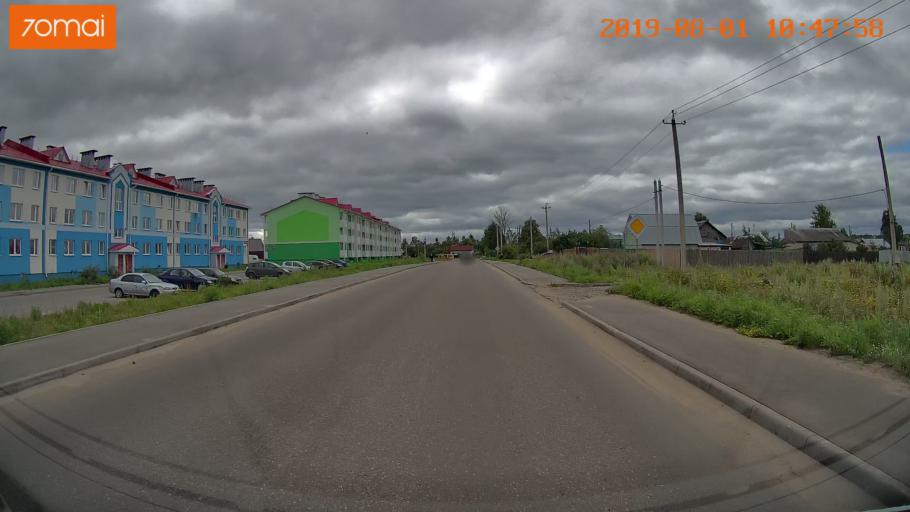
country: RU
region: Ivanovo
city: Kokhma
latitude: 56.9448
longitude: 41.0885
